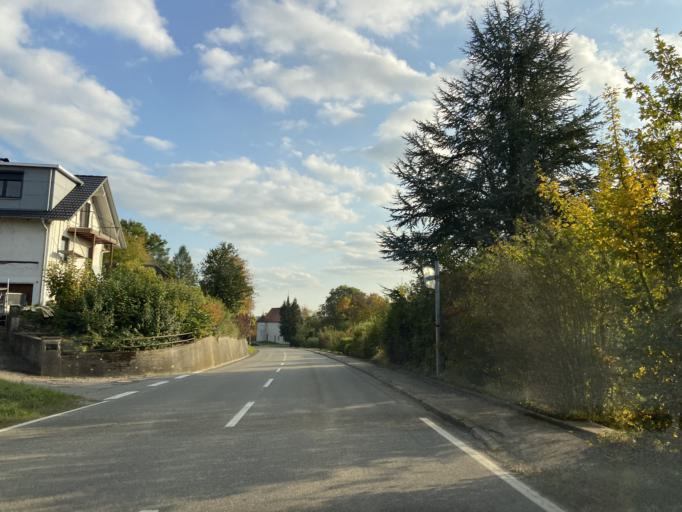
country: DE
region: Baden-Wuerttemberg
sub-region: Tuebingen Region
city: Scheer
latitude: 48.0788
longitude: 9.2939
